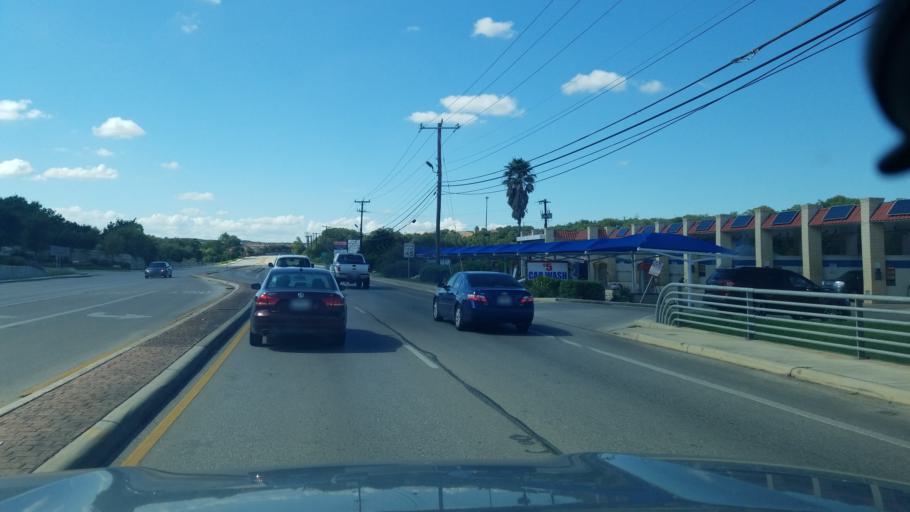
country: US
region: Texas
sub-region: Bexar County
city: Hollywood Park
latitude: 29.6215
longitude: -98.5135
